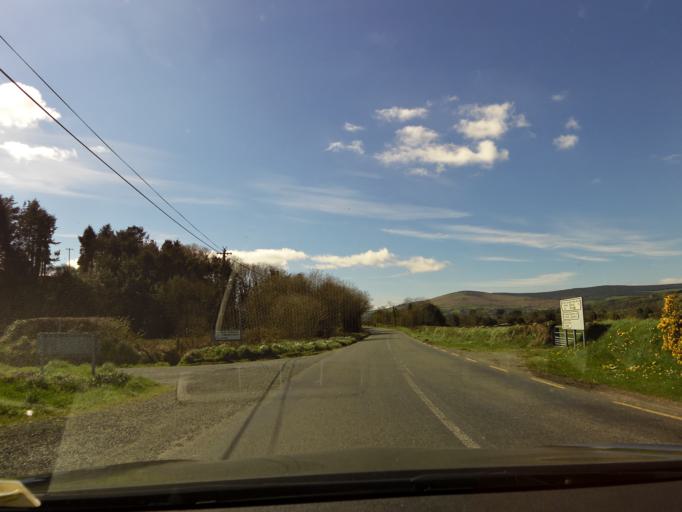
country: IE
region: Leinster
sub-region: Wicklow
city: Aughrim
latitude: 52.8217
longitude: -6.3803
